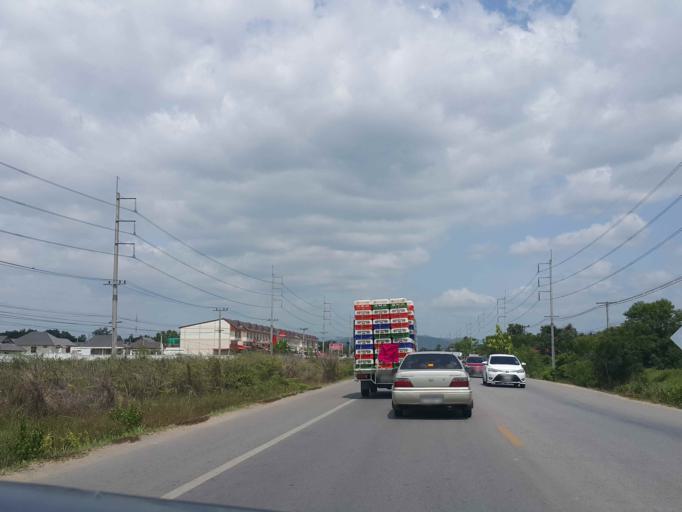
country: TH
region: Chiang Mai
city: Hang Dong
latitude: 18.7209
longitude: 98.9614
